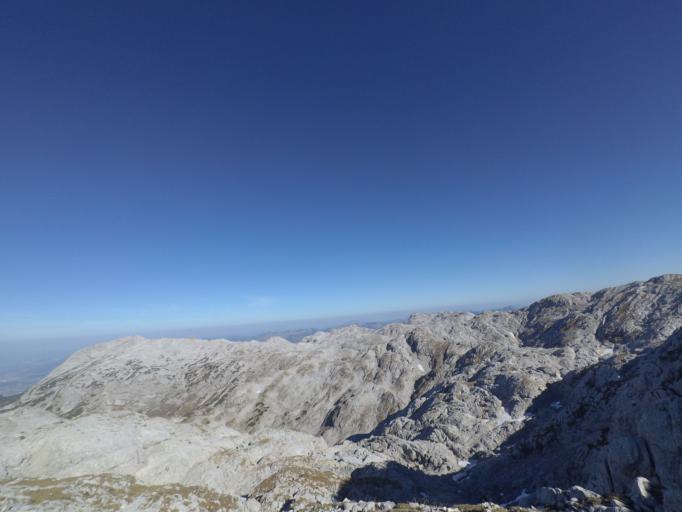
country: AT
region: Salzburg
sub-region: Politischer Bezirk Sankt Johann im Pongau
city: Werfenweng
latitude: 47.5012
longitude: 13.2344
